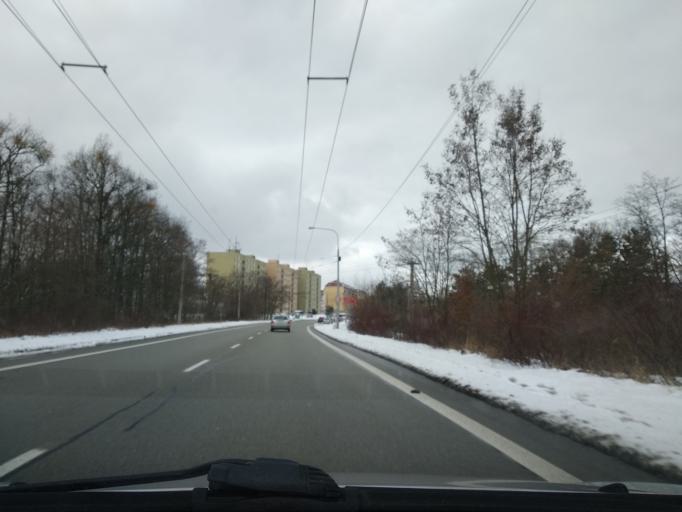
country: CZ
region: South Moravian
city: Ostopovice
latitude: 49.1867
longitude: 16.5371
